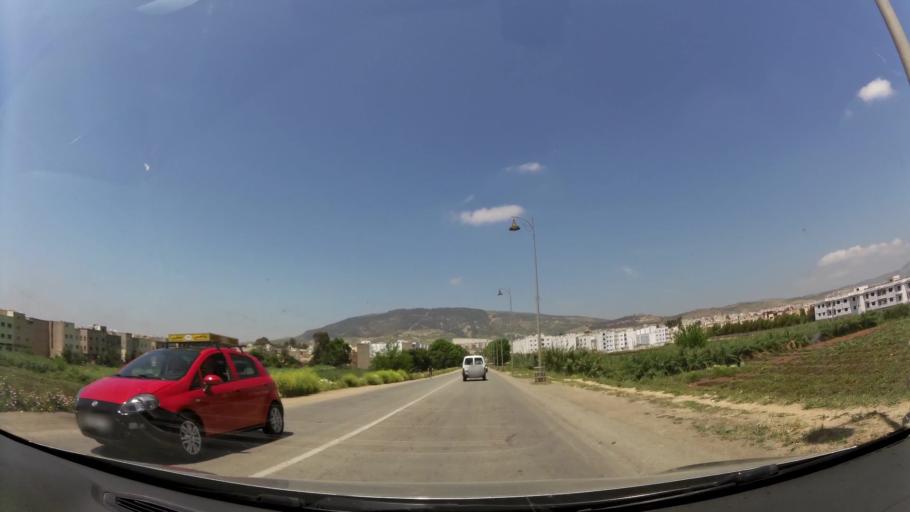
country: MA
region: Fes-Boulemane
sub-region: Fes
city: Fes
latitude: 34.0354
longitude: -5.0320
